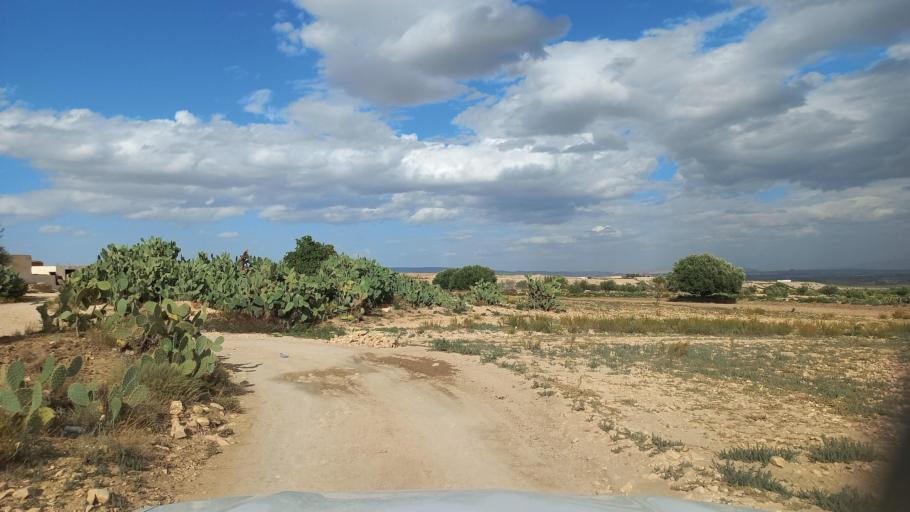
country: TN
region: Al Qasrayn
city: Sbiba
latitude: 35.4487
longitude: 9.0759
